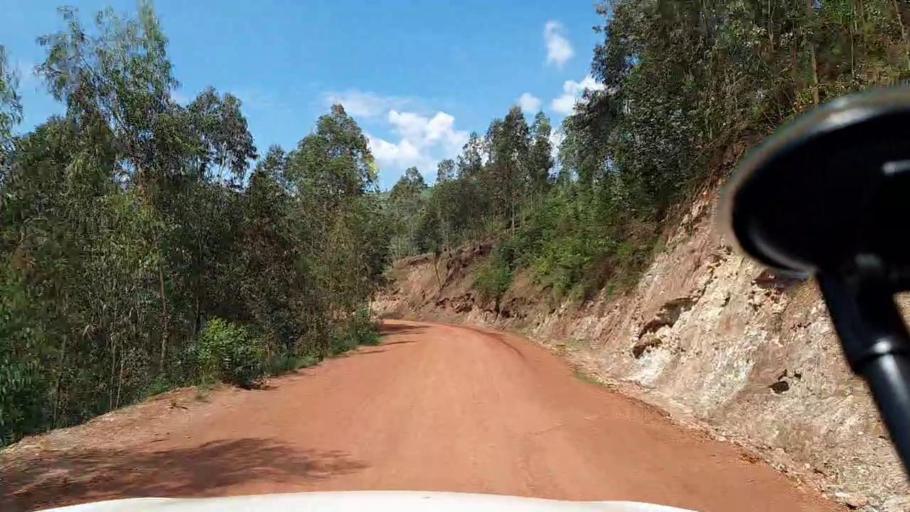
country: RW
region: Kigali
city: Kigali
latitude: -1.7998
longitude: 29.8885
